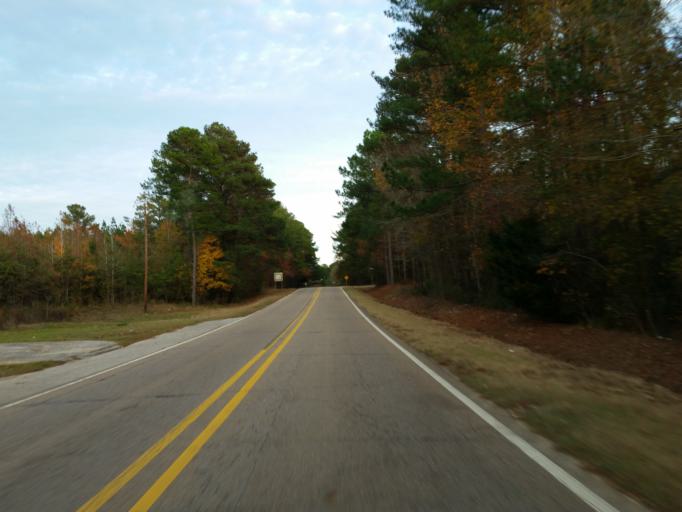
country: US
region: Alabama
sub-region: Sumter County
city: York
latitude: 32.4243
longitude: -88.4138
